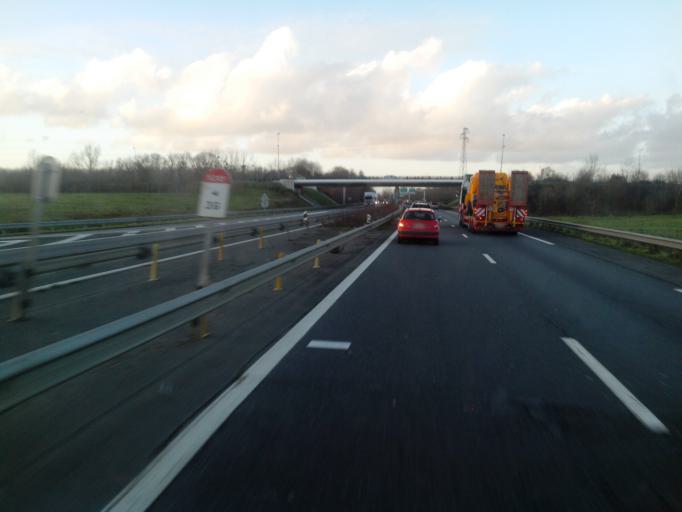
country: FR
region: Pays de la Loire
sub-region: Departement de la Loire-Atlantique
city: Basse-Goulaine
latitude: 47.2174
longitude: -1.4538
